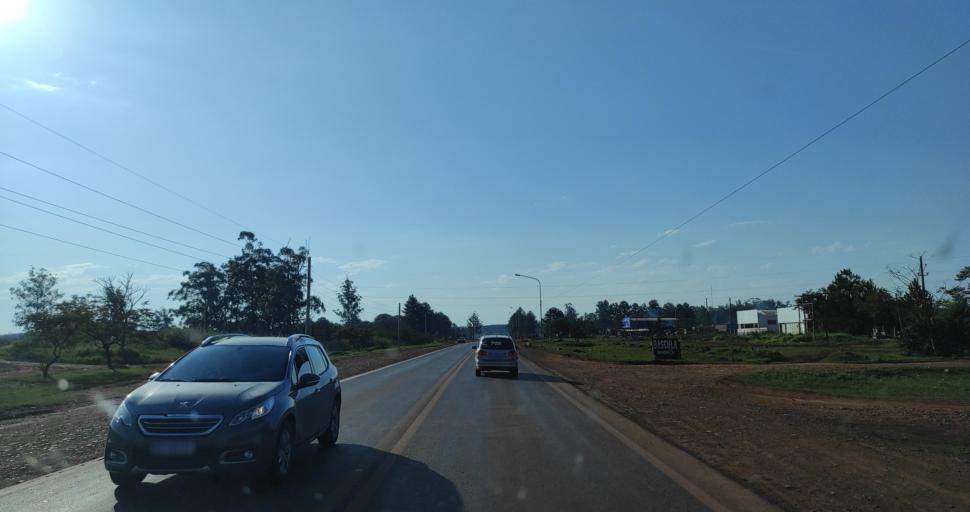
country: AR
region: Corrientes
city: Gobernador Ingeniero Valentin Virasoro
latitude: -28.0325
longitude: -56.0140
